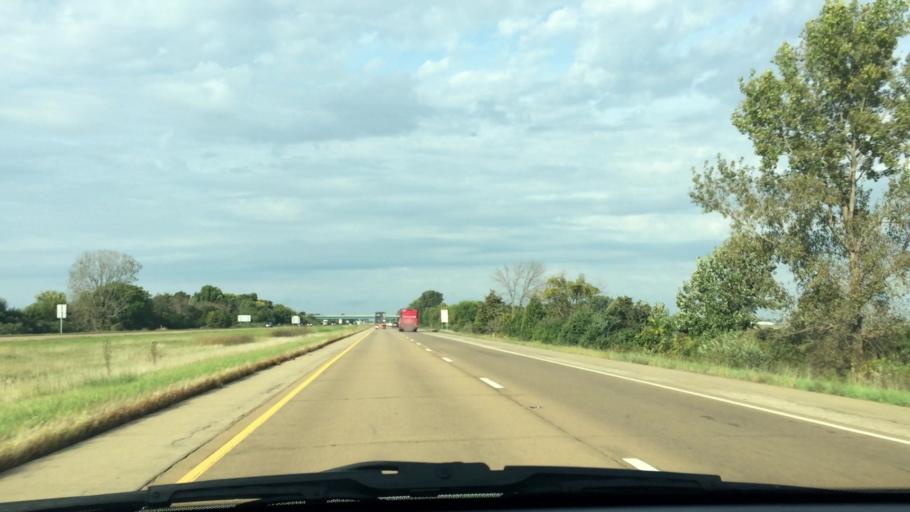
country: US
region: Illinois
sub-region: Whiteside County
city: Rock Falls
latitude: 41.7516
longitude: -89.7007
